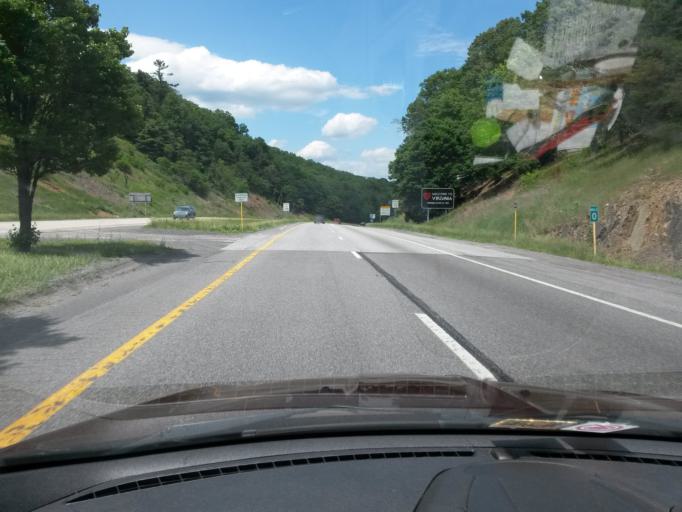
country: US
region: West Virginia
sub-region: Greenbrier County
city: White Sulphur Springs
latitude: 37.7874
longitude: -80.2243
